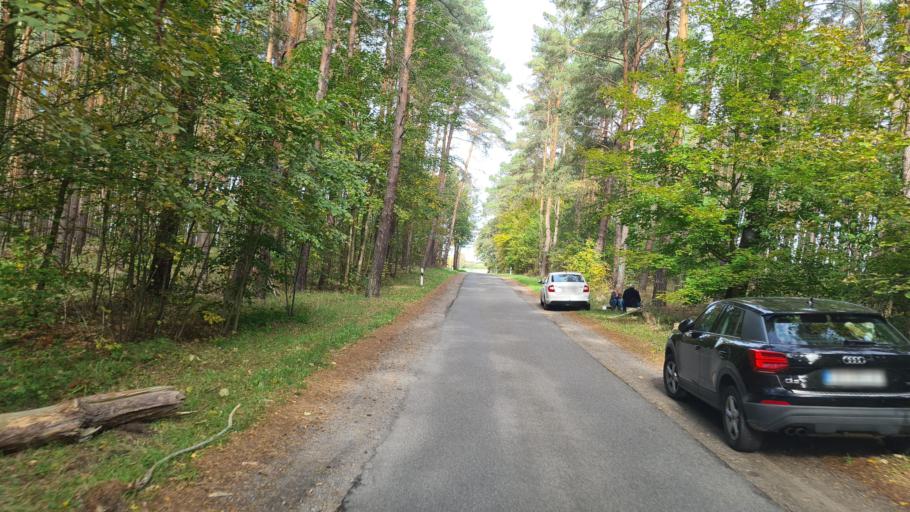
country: DE
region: Brandenburg
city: Linthe
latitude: 52.1024
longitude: 12.7561
